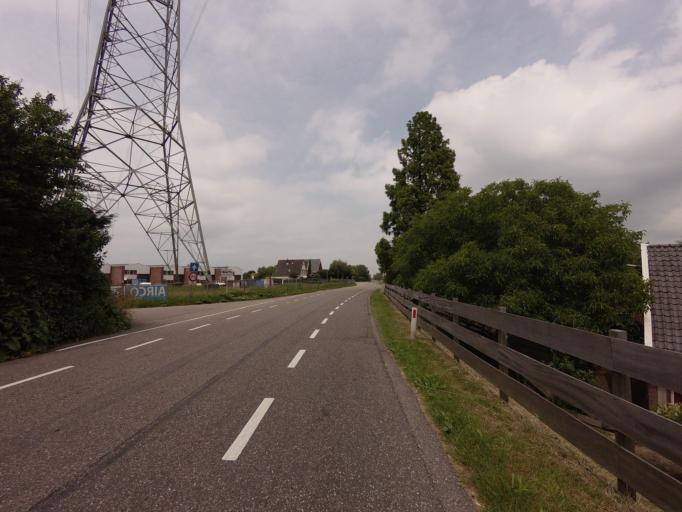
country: NL
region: South Holland
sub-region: Gemeente Krimpen aan den IJssel
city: Krimpen aan den IJssel
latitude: 51.9339
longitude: 4.6233
